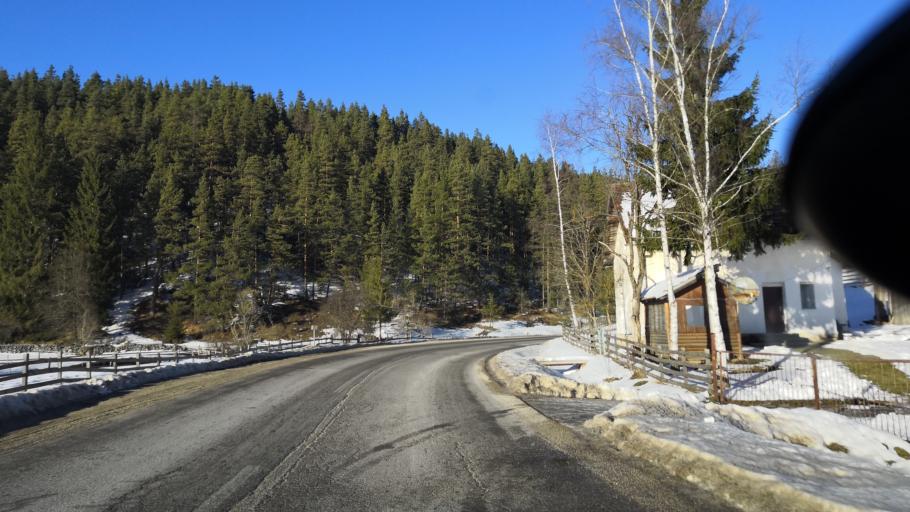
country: BA
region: Republika Srpska
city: Sokolac
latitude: 43.9785
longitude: 18.8581
